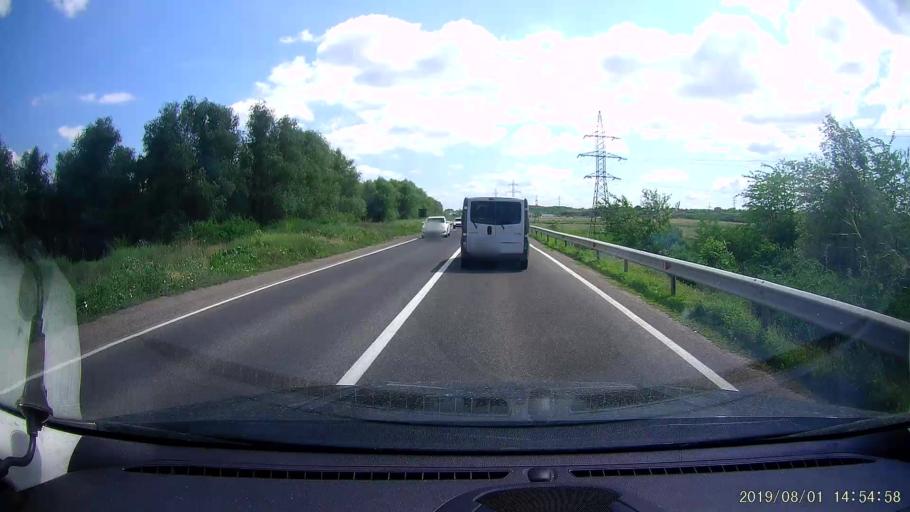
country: RO
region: Braila
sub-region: Municipiul Braila
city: Braila
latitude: 45.3107
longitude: 27.9830
